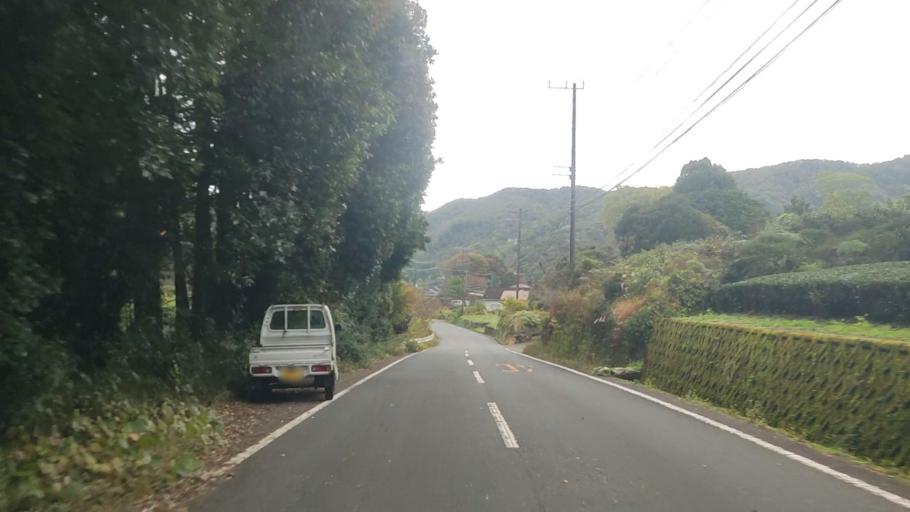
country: JP
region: Shizuoka
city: Ito
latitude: 34.9331
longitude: 138.9939
